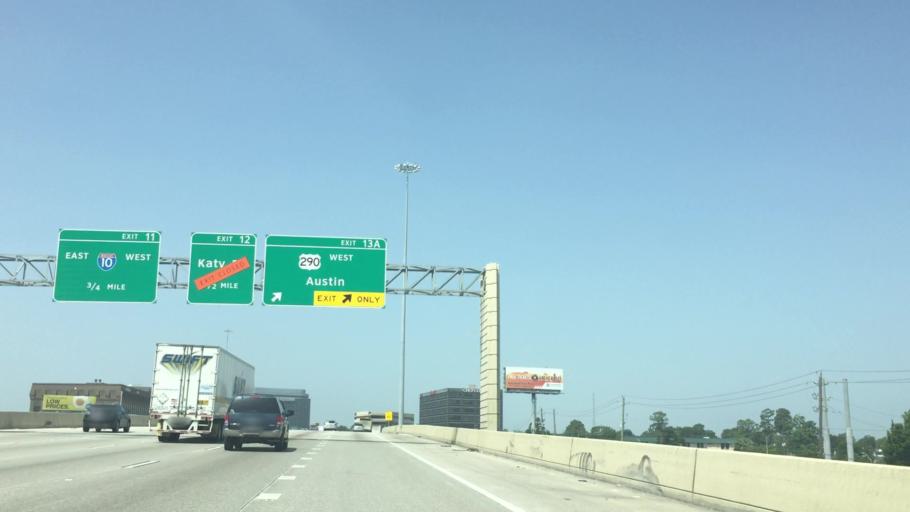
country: US
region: Texas
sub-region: Harris County
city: Spring Valley
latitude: 29.8098
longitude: -95.4394
